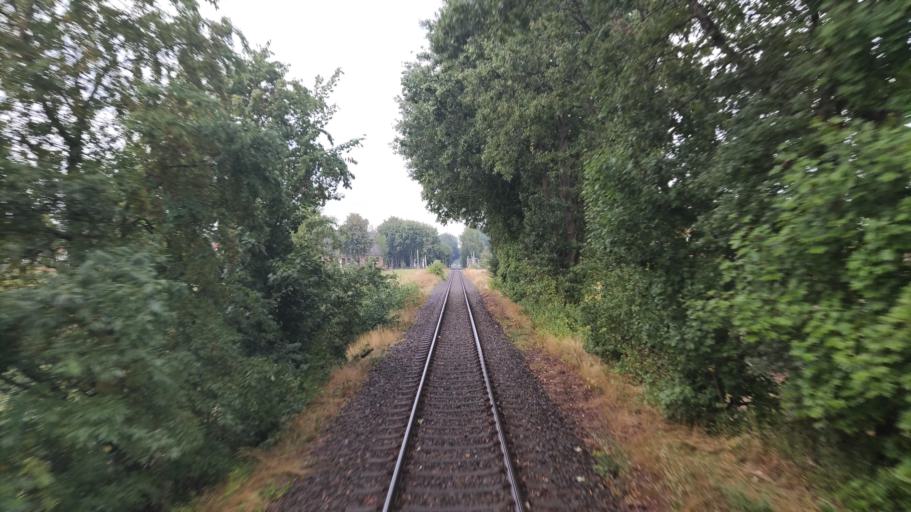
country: DE
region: Lower Saxony
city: Bispingen
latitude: 53.0792
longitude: 9.9919
